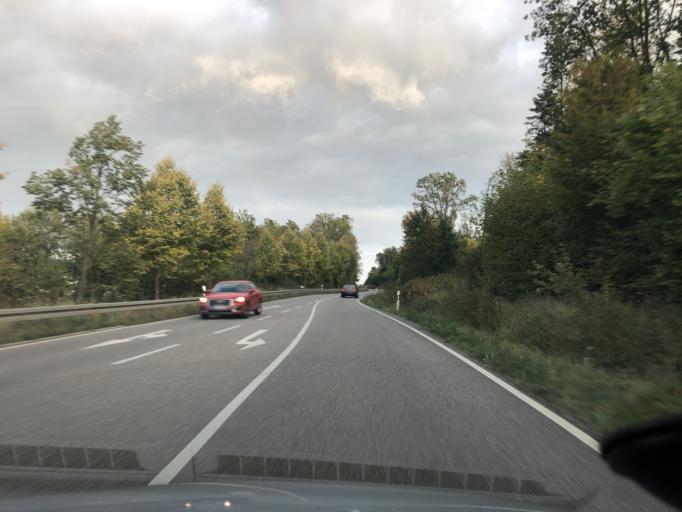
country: DE
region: Baden-Wuerttemberg
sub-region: Karlsruhe Region
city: Wimsheim
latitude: 48.8440
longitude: 8.8258
